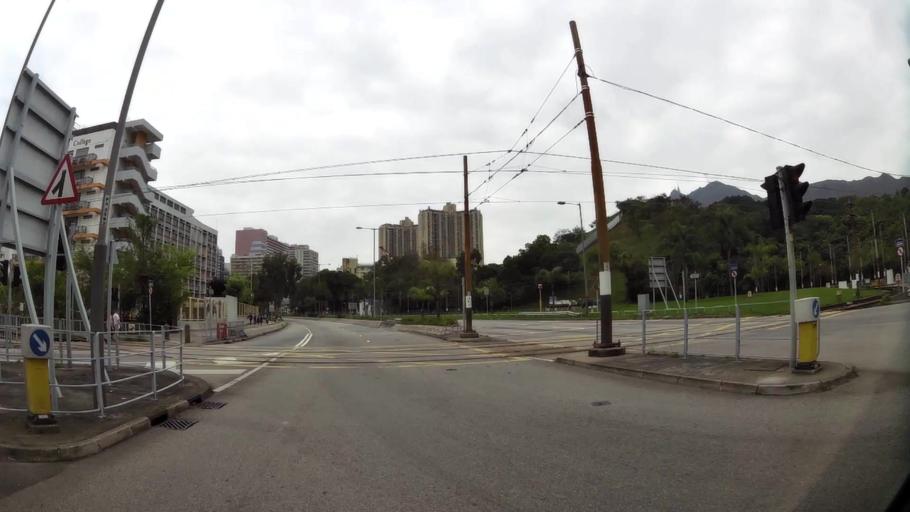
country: HK
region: Tuen Mun
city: Tuen Mun
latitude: 22.4047
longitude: 113.9671
